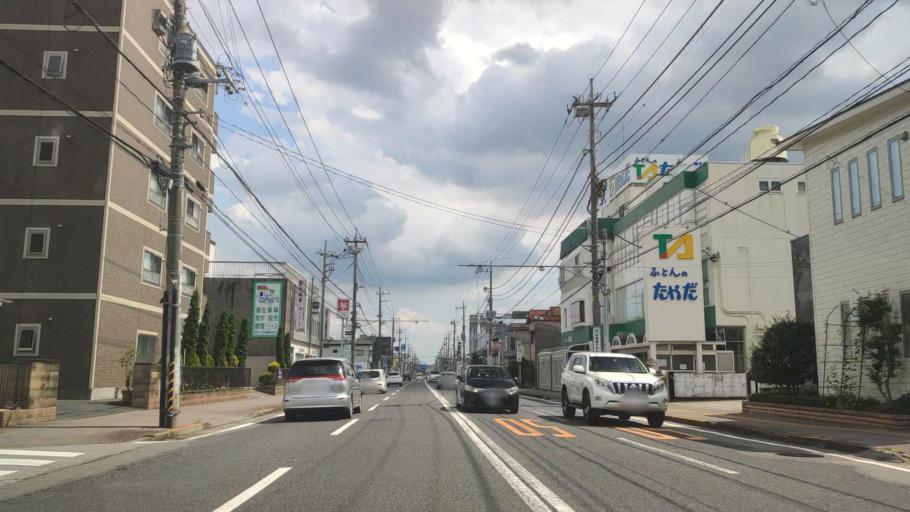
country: JP
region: Tochigi
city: Utsunomiya-shi
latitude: 36.5811
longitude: 139.8687
